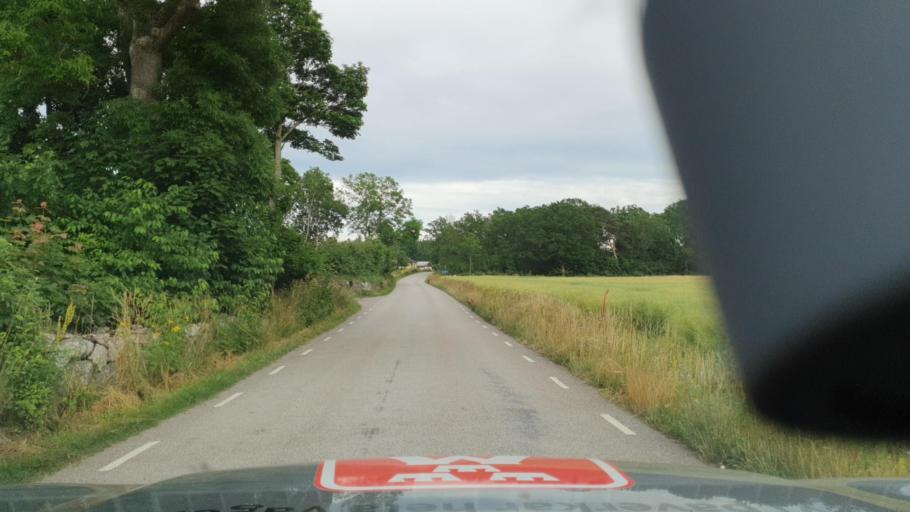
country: SE
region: Kalmar
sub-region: Kalmar Kommun
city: Ljungbyholm
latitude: 56.5888
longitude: 16.1056
